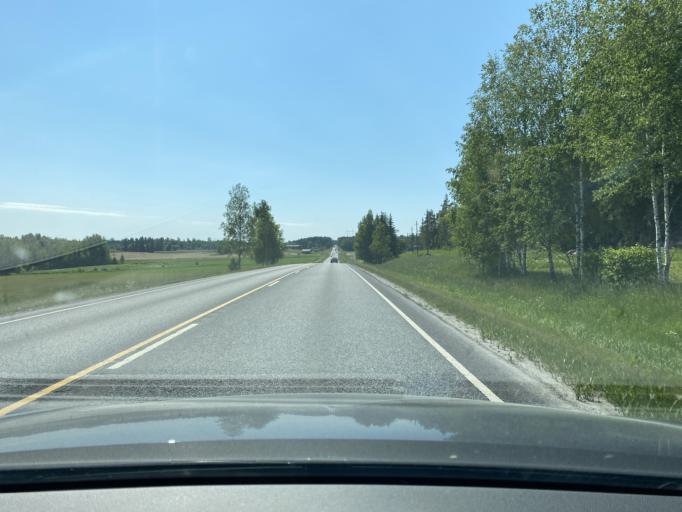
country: FI
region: Pirkanmaa
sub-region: Tampere
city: Nokia
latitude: 61.4203
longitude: 23.3301
